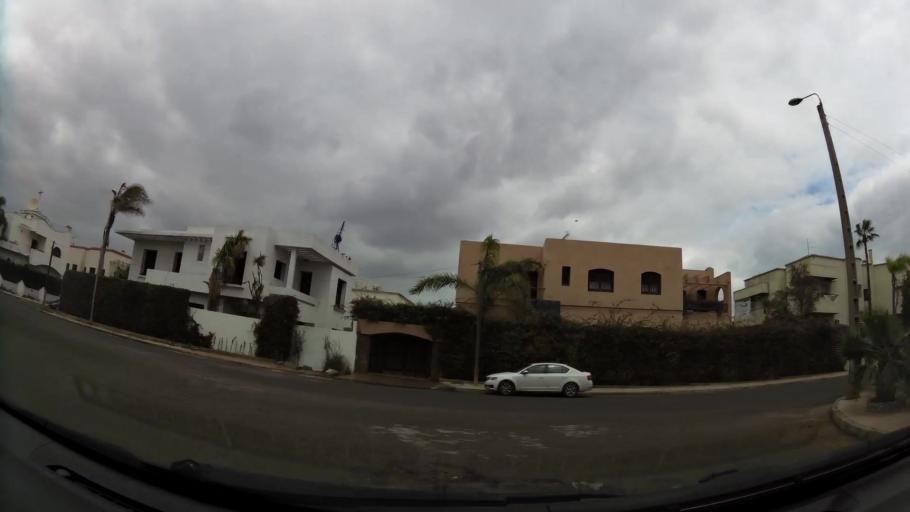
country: MA
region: Grand Casablanca
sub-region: Casablanca
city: Casablanca
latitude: 33.5554
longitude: -7.6215
